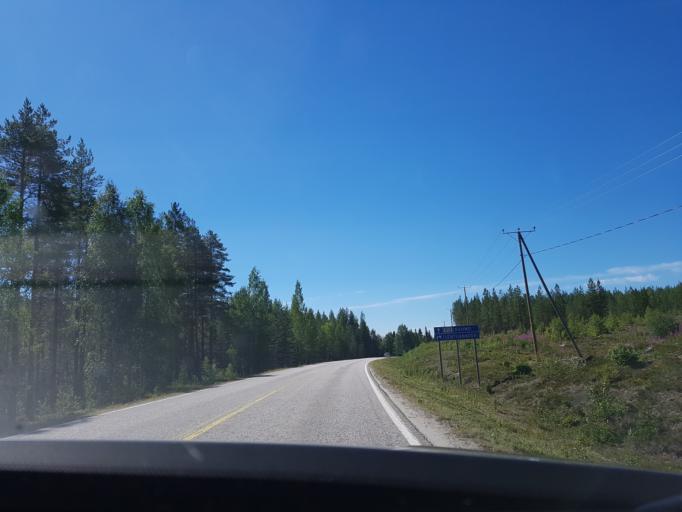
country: FI
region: Kainuu
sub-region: Kehys-Kainuu
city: Kuhmo
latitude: 64.1717
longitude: 29.6585
